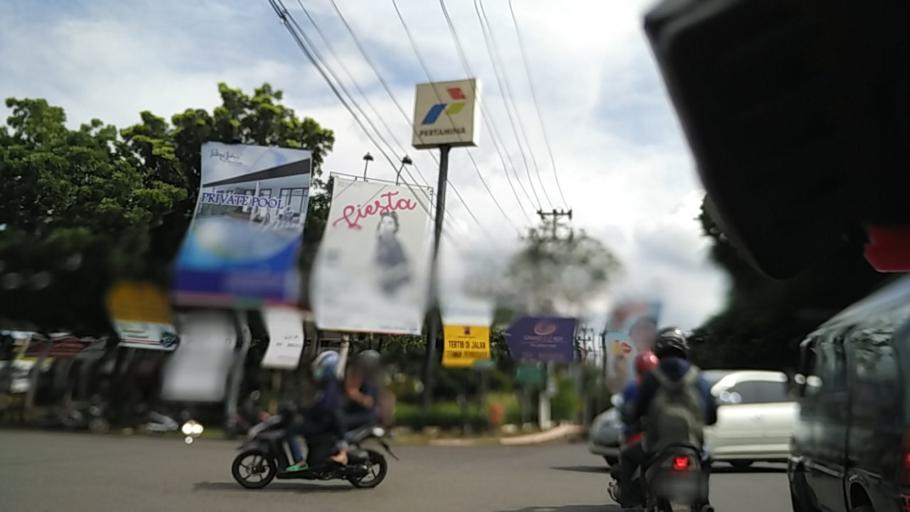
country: ID
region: Central Java
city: Semarang
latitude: -7.0155
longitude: 110.4183
